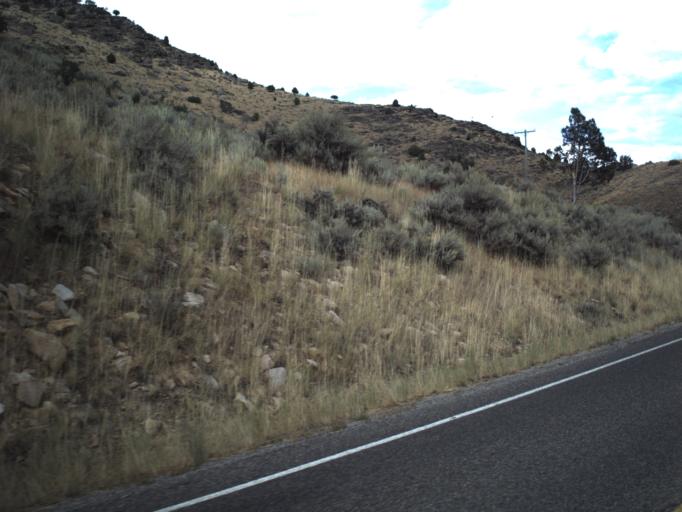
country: US
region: Utah
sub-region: Cache County
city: Millville
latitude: 41.6053
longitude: -111.5961
